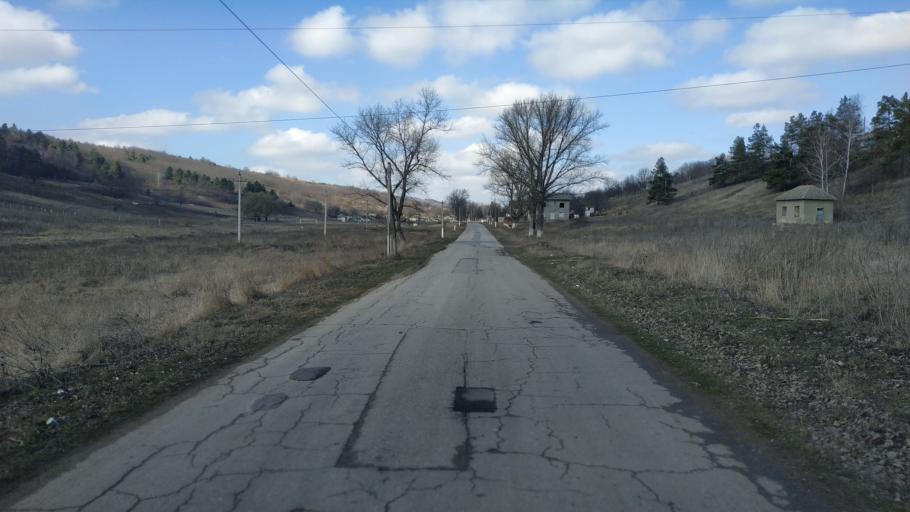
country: MD
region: Hincesti
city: Hincesti
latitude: 46.8708
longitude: 28.6363
